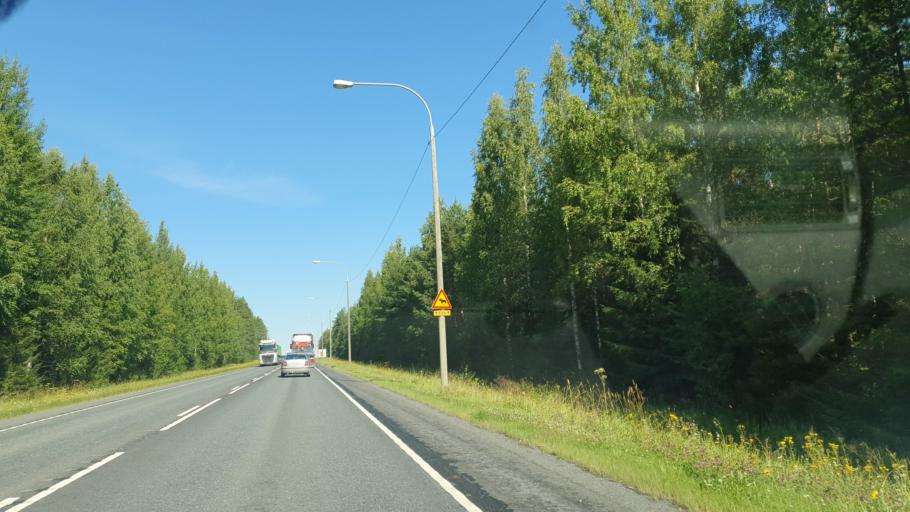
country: FI
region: Northern Savo
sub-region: Ylae-Savo
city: Lapinlahti
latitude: 63.2651
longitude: 27.4671
